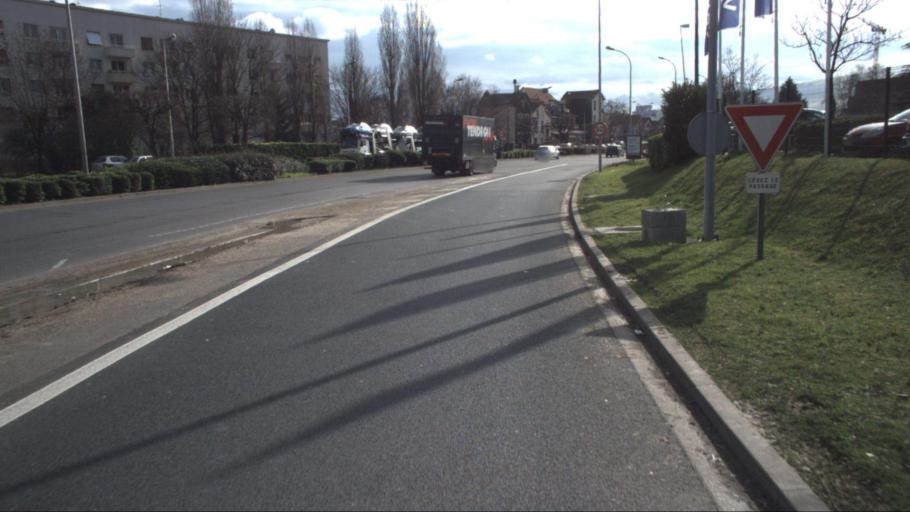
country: FR
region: Ile-de-France
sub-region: Departement du Val-de-Marne
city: Fontenay-sous-Bois
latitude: 48.8594
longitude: 2.4901
